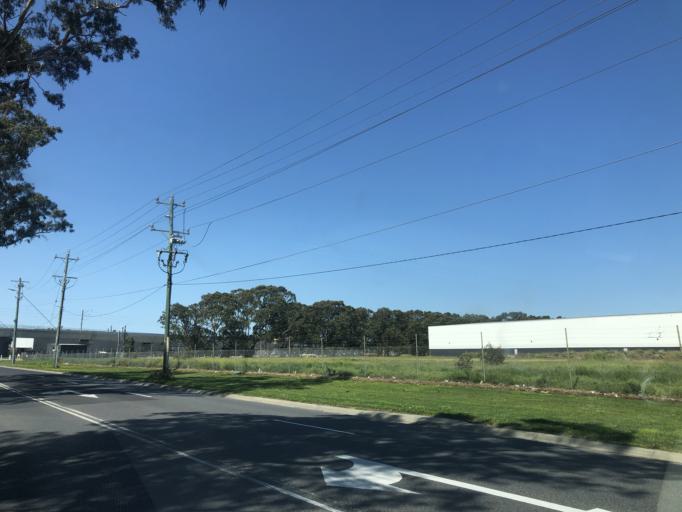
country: AU
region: Victoria
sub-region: Casey
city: Hampton Park
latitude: -38.0346
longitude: 145.2364
